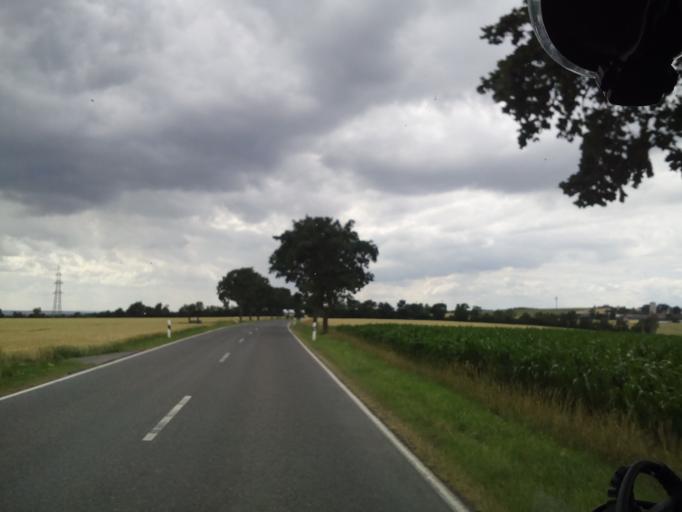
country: DE
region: Bavaria
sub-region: Upper Franconia
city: Sonnefeld
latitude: 50.2490
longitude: 11.0958
